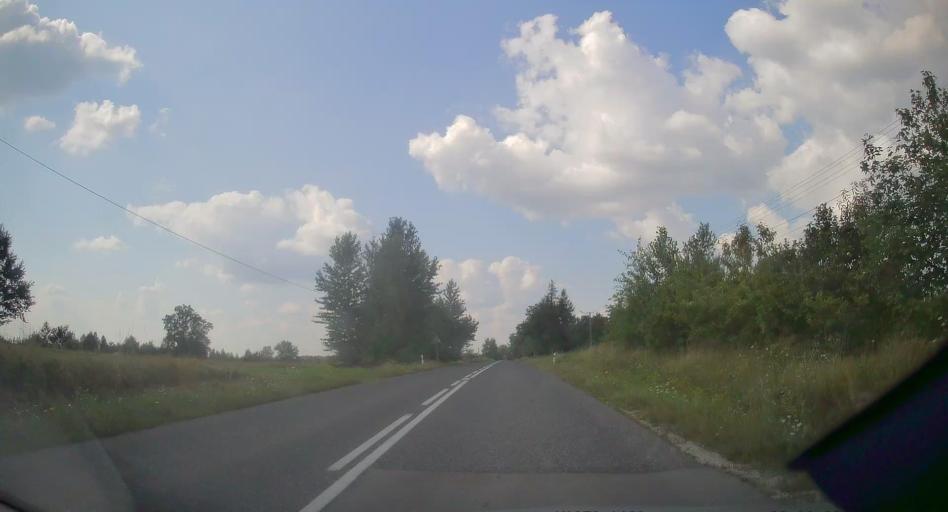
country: PL
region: Swietokrzyskie
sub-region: Powiat kielecki
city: Lopuszno
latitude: 50.9164
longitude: 20.2431
